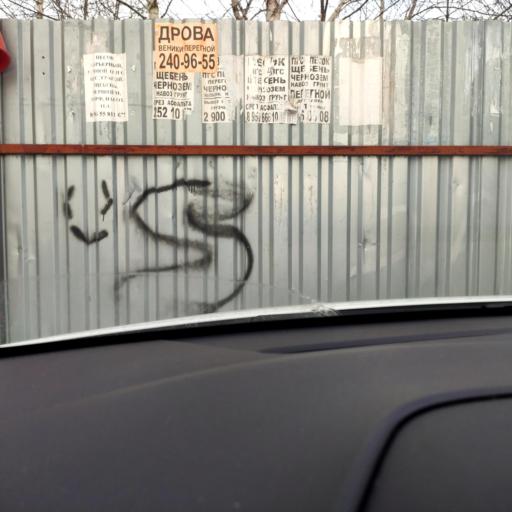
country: RU
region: Tatarstan
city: Osinovo
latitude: 55.8681
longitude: 48.8619
